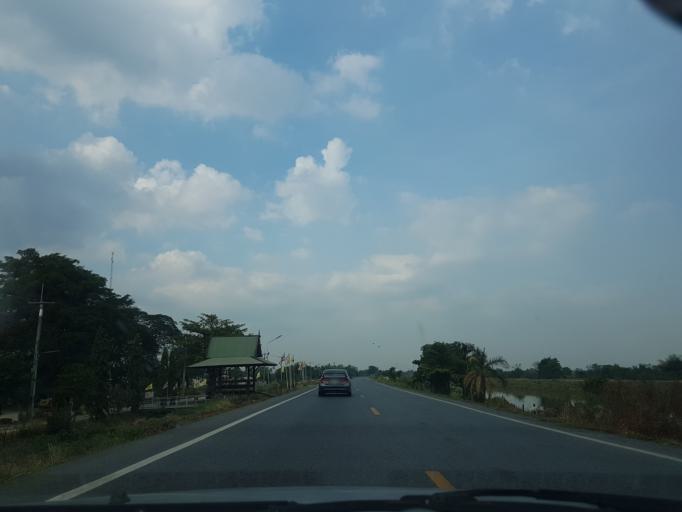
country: TH
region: Phra Nakhon Si Ayutthaya
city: Phachi
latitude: 14.4905
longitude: 100.7368
